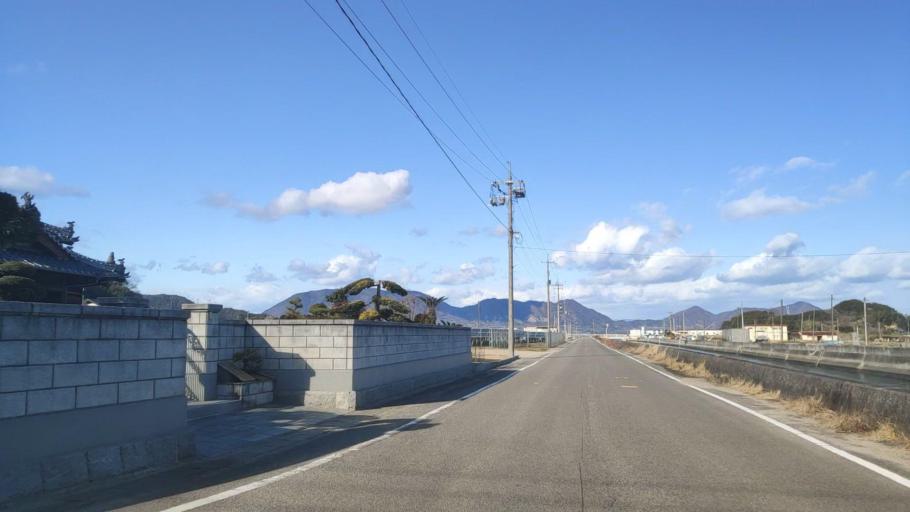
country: JP
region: Hiroshima
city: Innoshima
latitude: 34.2111
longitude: 133.1225
